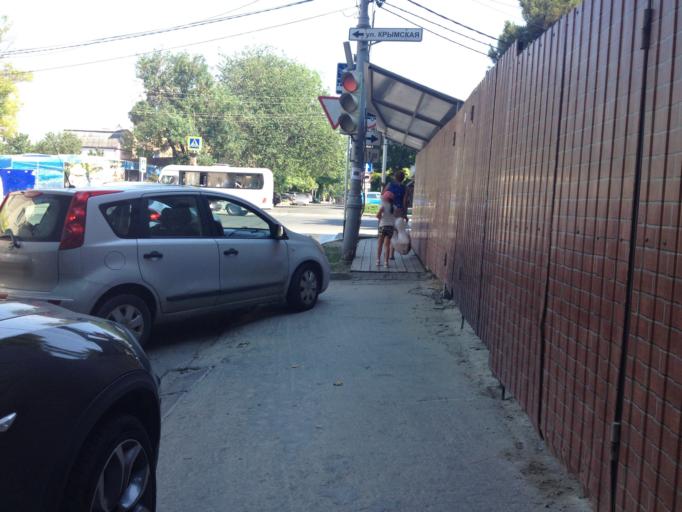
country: RU
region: Krasnodarskiy
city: Anapa
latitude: 44.8926
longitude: 37.3130
